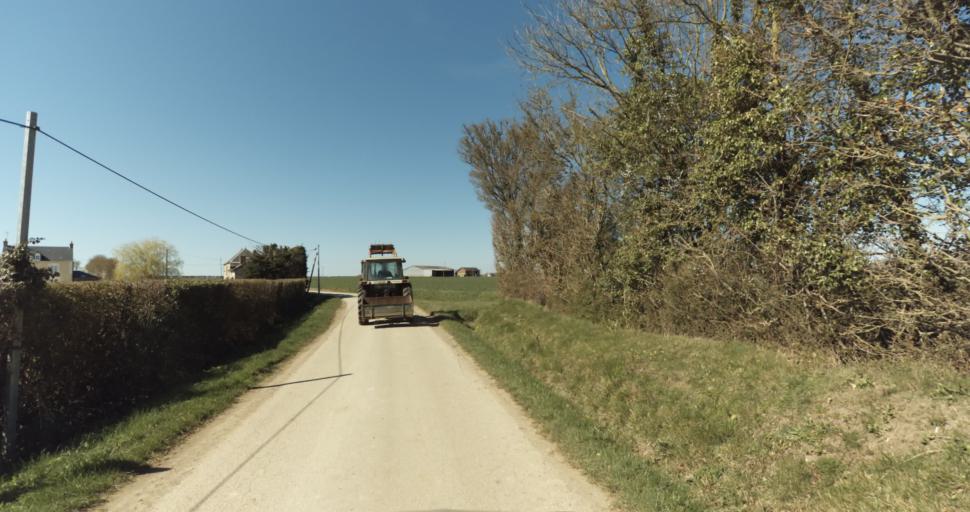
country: FR
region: Lower Normandy
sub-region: Departement du Calvados
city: Saint-Pierre-sur-Dives
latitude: 49.0365
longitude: 0.0041
